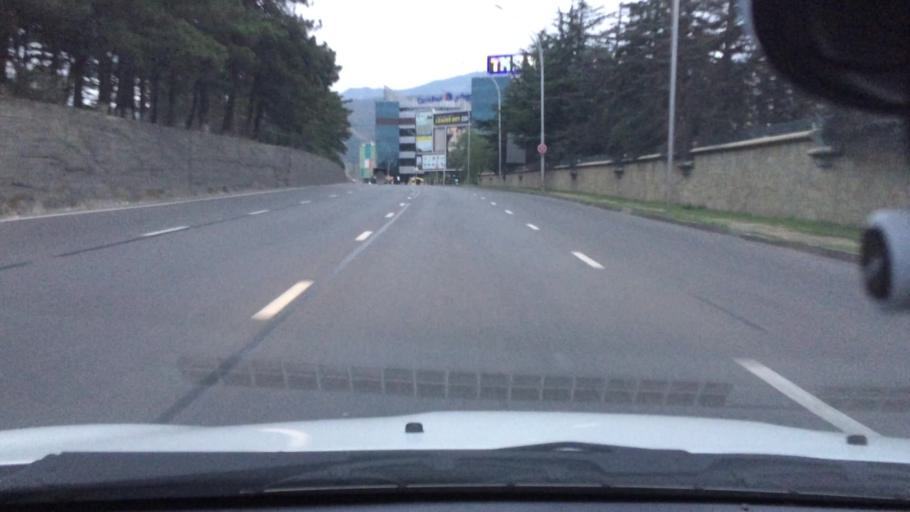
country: GE
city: Zahesi
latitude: 41.8131
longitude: 44.7722
